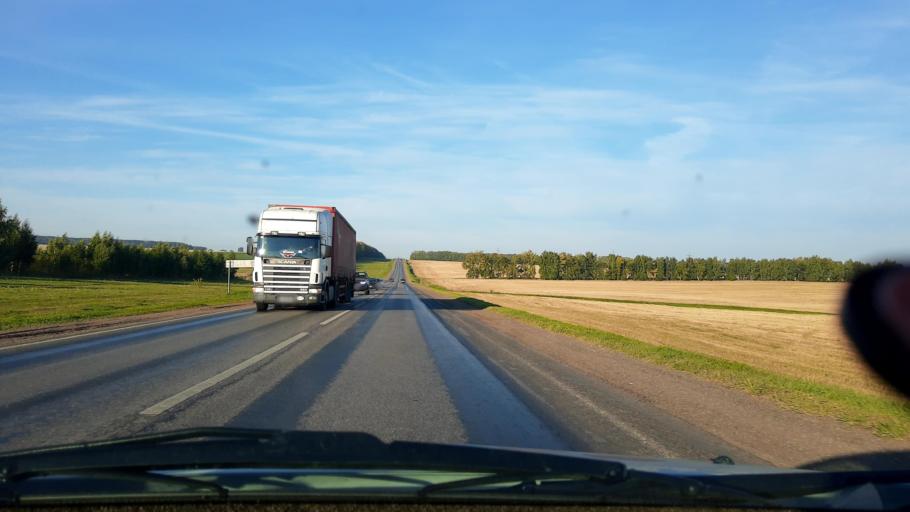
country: RU
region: Bashkortostan
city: Ulukulevo
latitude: 54.4032
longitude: 56.2908
